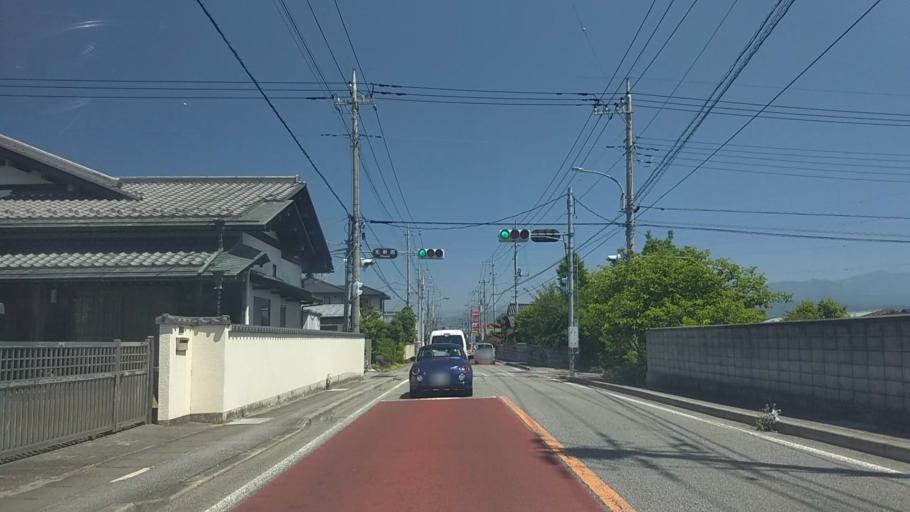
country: JP
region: Yamanashi
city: Ryuo
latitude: 35.6585
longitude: 138.4649
